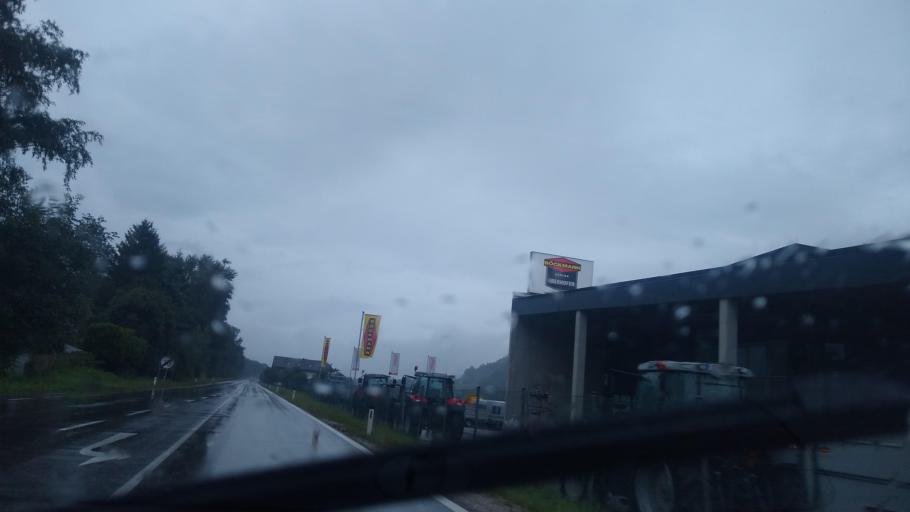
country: AT
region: Tyrol
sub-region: Politischer Bezirk Schwaz
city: Stans
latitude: 47.3633
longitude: 11.7289
